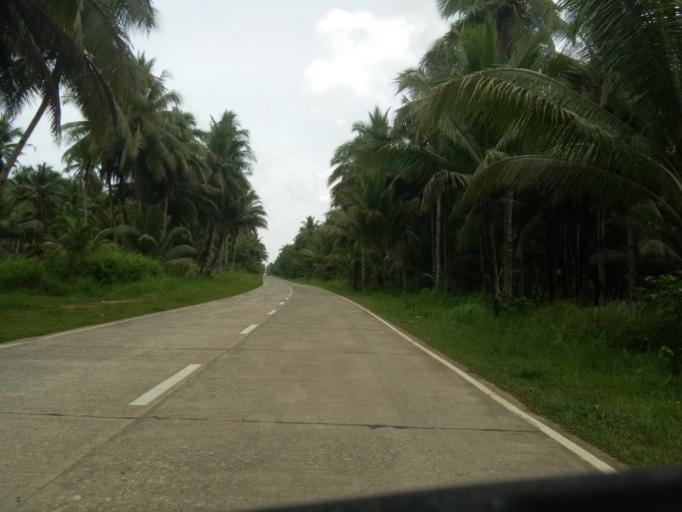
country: PH
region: Caraga
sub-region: Province of Surigao del Norte
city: San Isidro
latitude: 9.9251
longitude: 126.0524
